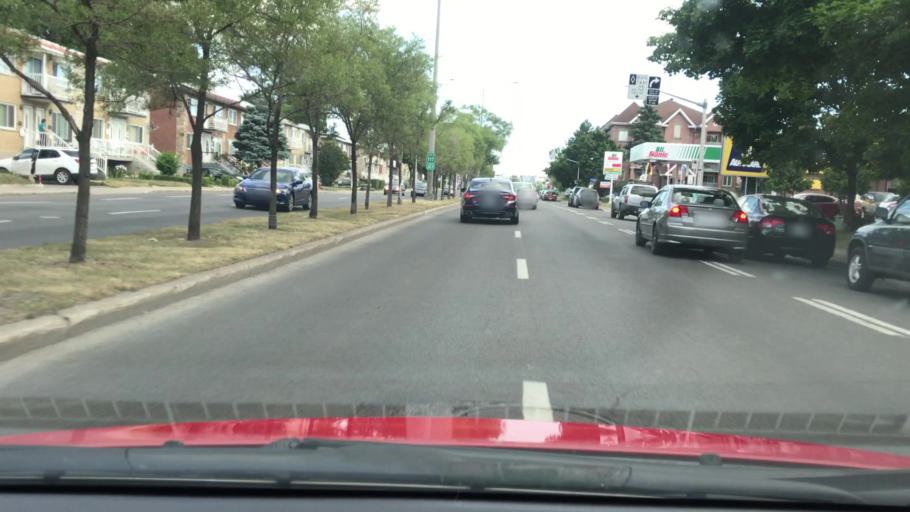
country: CA
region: Quebec
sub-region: Laval
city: Laval
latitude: 45.5412
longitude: -73.7362
